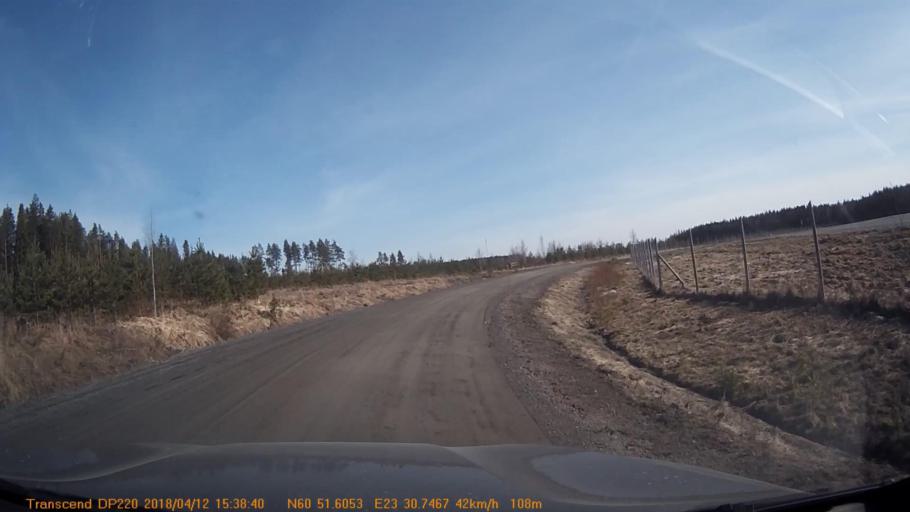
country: FI
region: Haeme
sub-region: Forssa
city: Jokioinen
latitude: 60.8599
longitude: 23.5131
